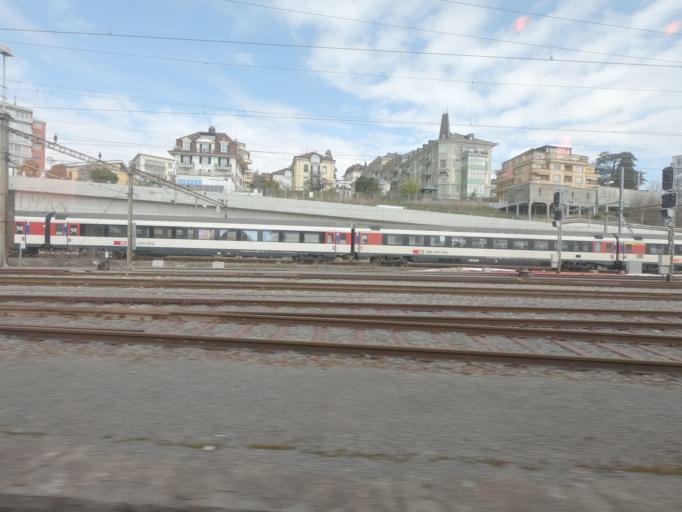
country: CH
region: Vaud
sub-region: Lausanne District
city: Lausanne
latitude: 46.5184
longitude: 6.6205
